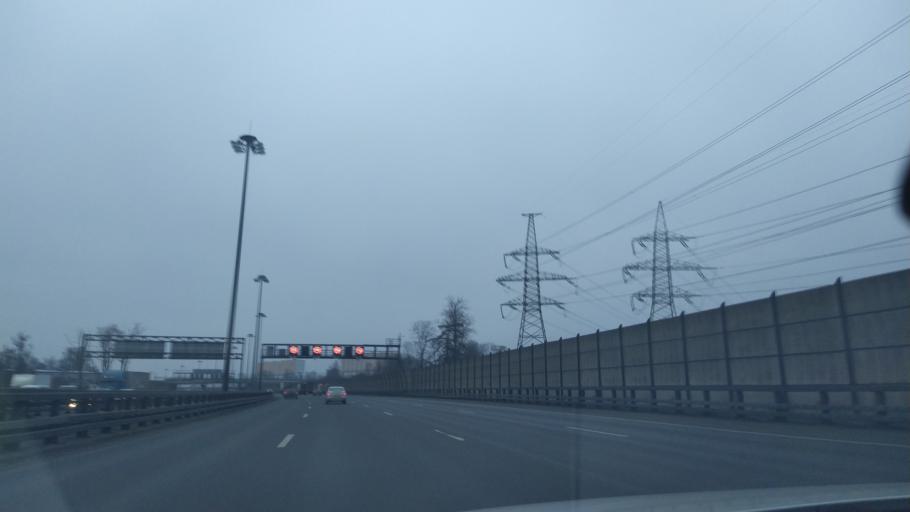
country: RU
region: St.-Petersburg
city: Krasnogvargeisky
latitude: 59.9845
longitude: 30.4949
